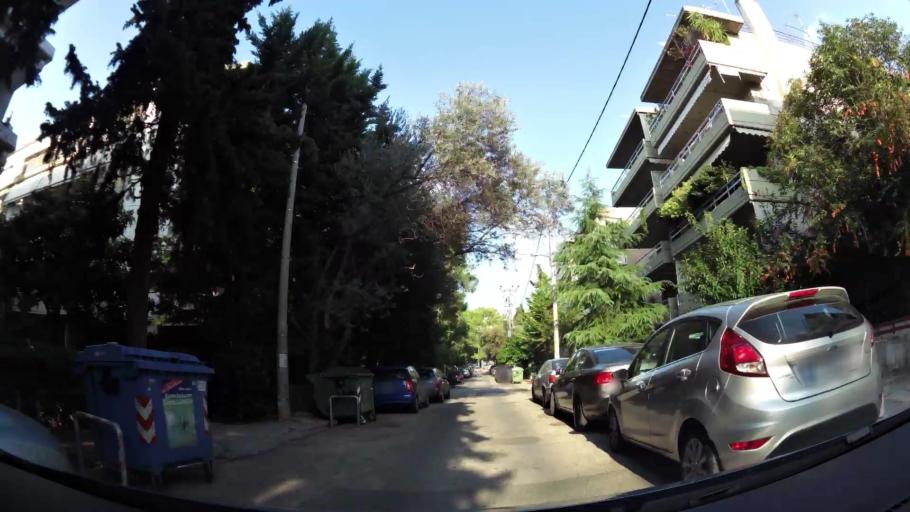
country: GR
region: Attica
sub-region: Nomarchia Athinas
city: Agia Paraskevi
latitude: 38.0039
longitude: 23.8287
